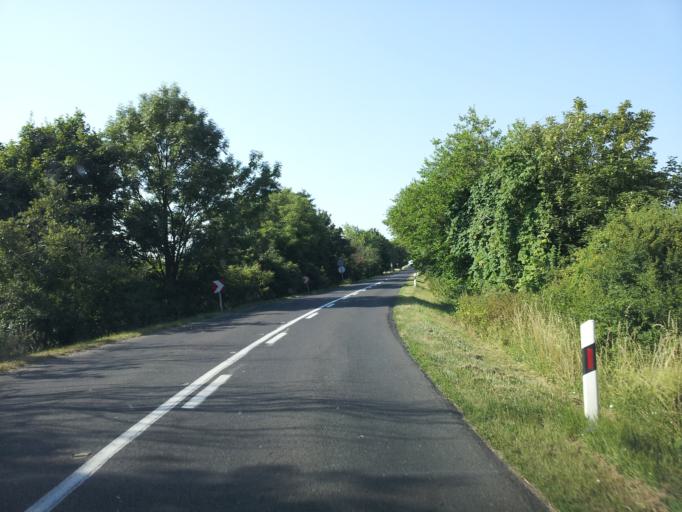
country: HU
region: Fejer
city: Bicske
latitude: 47.4036
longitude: 18.5863
